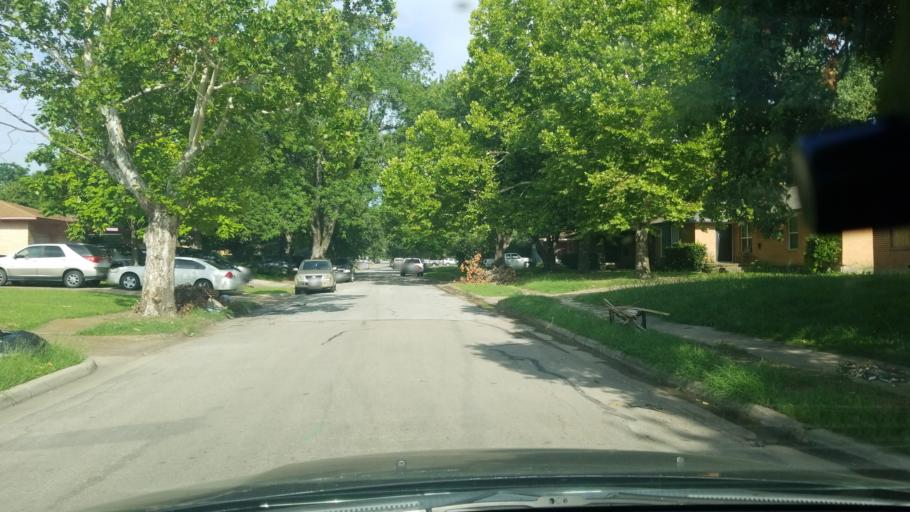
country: US
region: Texas
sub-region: Dallas County
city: Balch Springs
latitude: 32.7477
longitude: -96.6629
